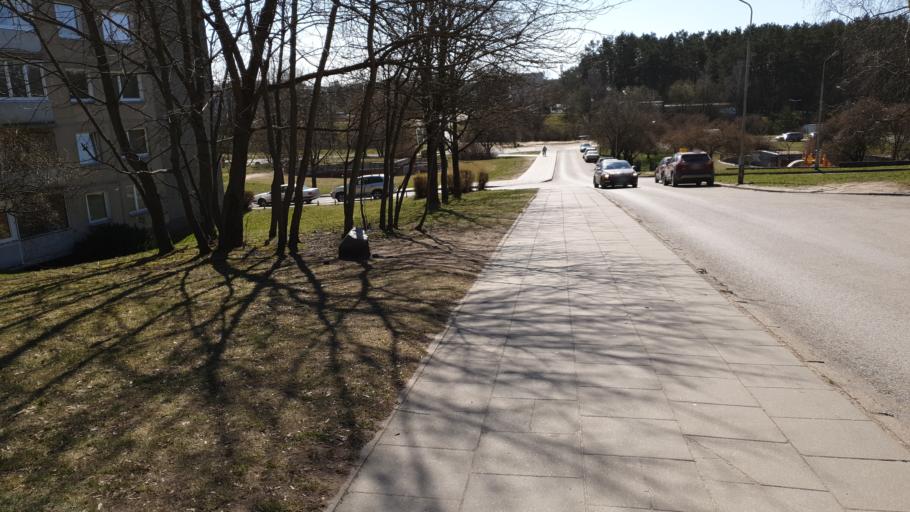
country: LT
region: Vilnius County
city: Lazdynai
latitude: 54.6726
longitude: 25.2144
